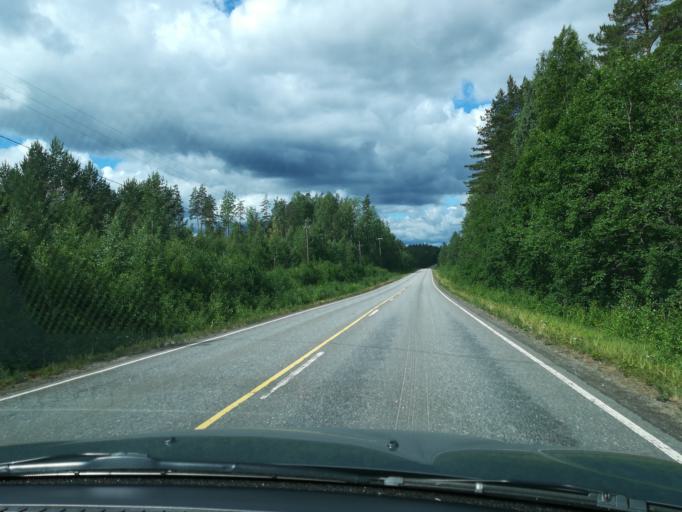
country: FI
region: Southern Savonia
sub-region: Mikkeli
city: Maentyharju
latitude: 61.3645
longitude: 26.9695
